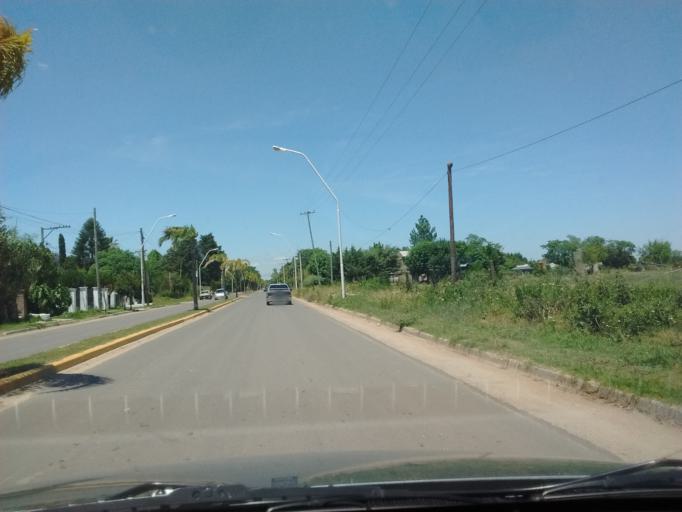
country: AR
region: Entre Rios
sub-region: Departamento de Gualeguay
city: Gualeguay
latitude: -33.1320
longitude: -59.3236
